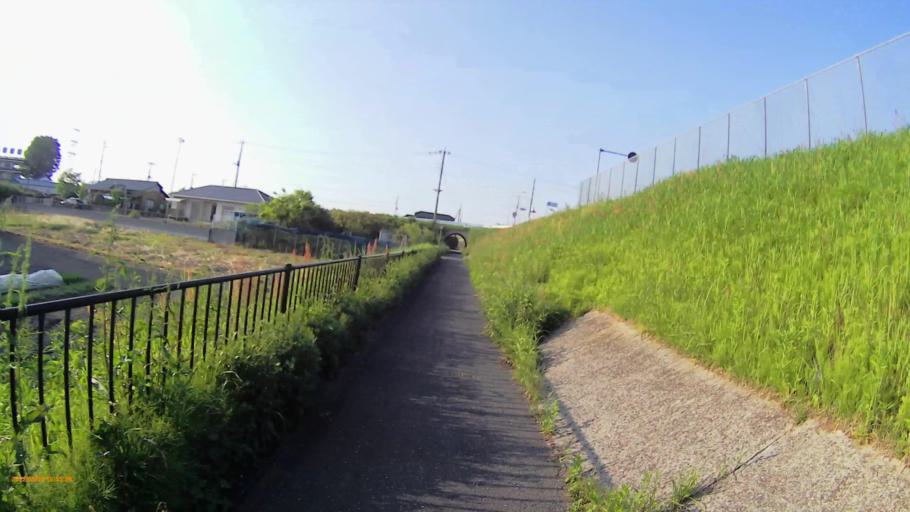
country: JP
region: Saitama
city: Kurihashi
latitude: 36.1087
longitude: 139.7234
